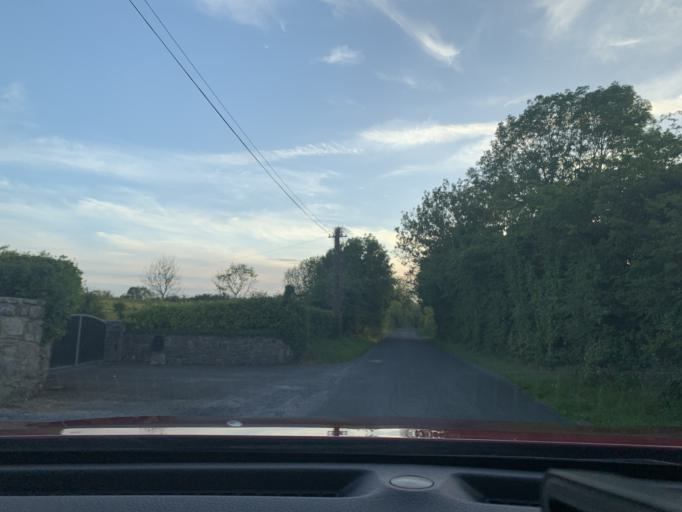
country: IE
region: Connaught
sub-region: Sligo
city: Sligo
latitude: 54.2899
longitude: -8.4522
